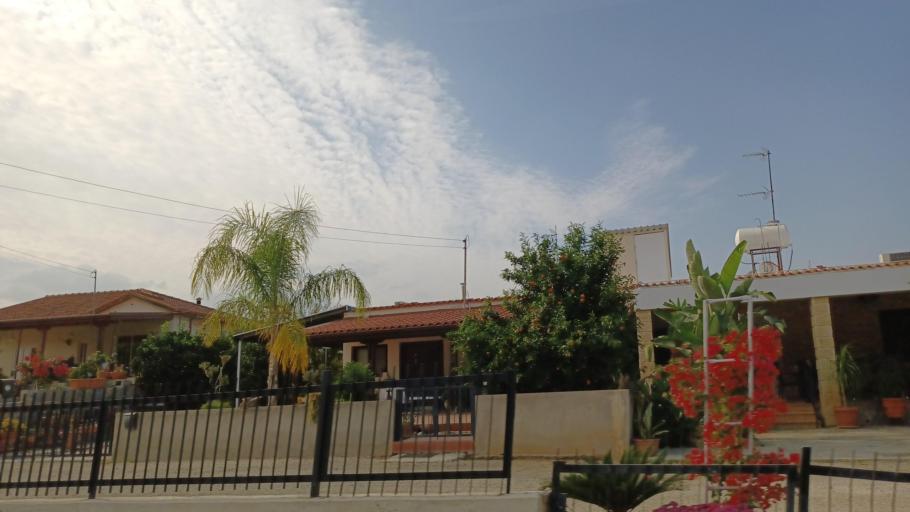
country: CY
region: Lefkosia
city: Kakopetria
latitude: 35.0370
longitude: 32.9027
